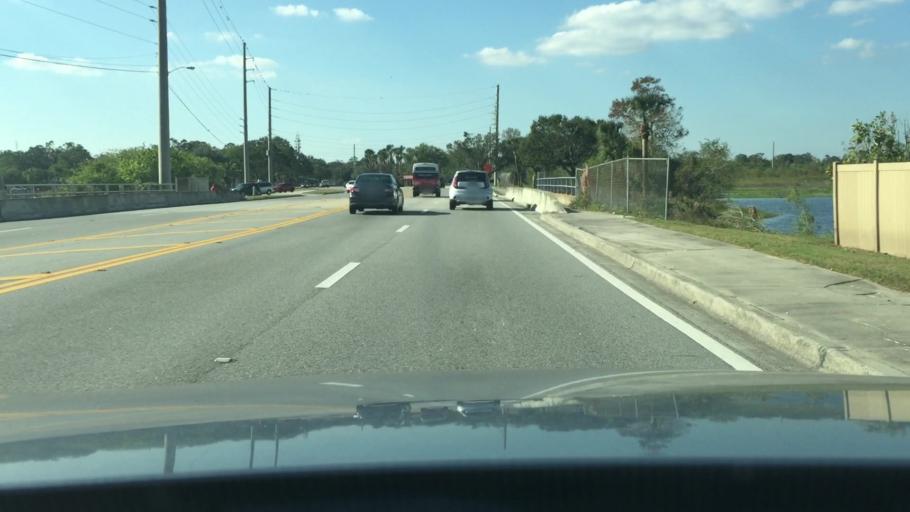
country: US
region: Florida
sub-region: Osceola County
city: Kissimmee
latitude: 28.2929
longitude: -81.3948
